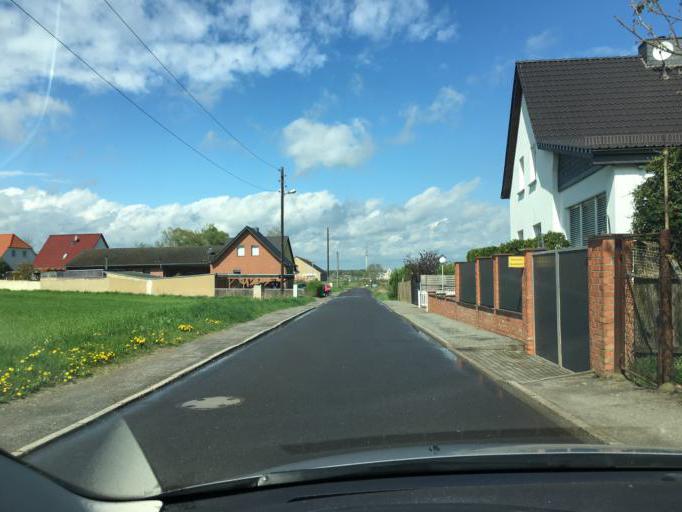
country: DE
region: Saxony-Anhalt
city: Haldensleben I
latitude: 52.2695
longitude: 11.4165
